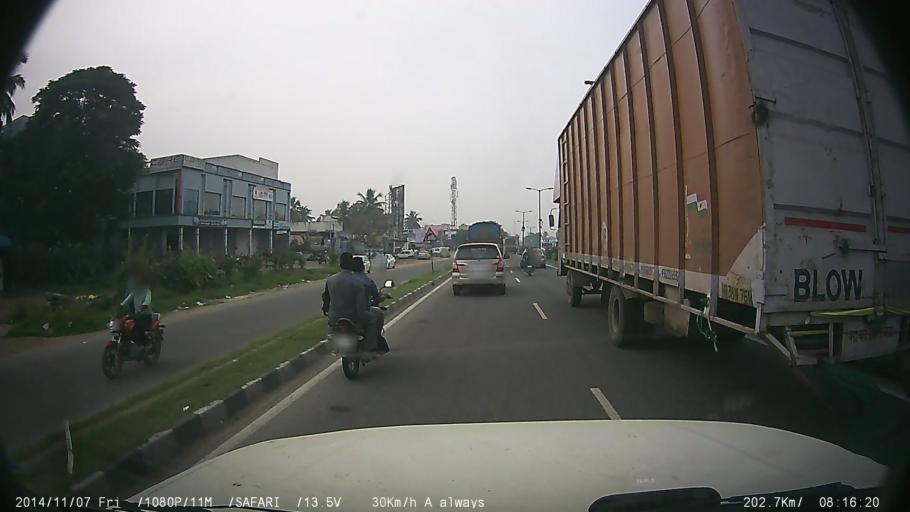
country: IN
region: Tamil Nadu
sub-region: Salem
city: Salem
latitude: 11.6751
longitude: 78.1280
